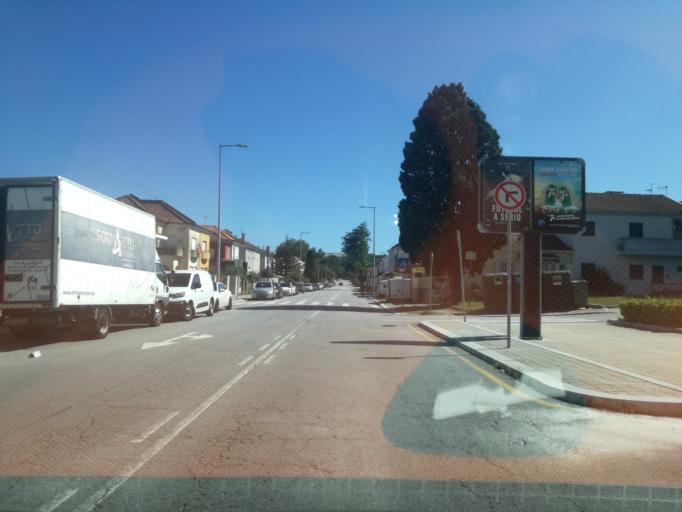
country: PT
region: Porto
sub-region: Matosinhos
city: Sao Mamede de Infesta
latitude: 41.1814
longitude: -8.6093
